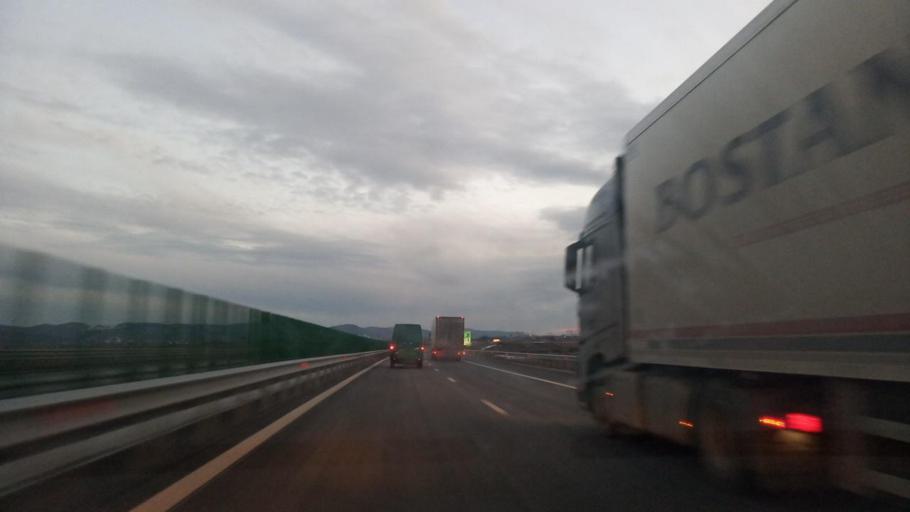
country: RO
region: Bacau
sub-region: Comuna Saucesti
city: Saucesti
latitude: 46.6158
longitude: 26.9565
